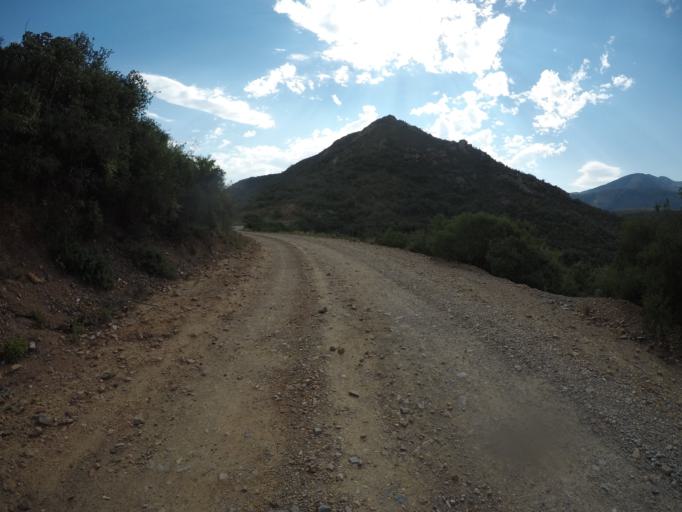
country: ZA
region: Eastern Cape
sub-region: Cacadu District Municipality
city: Kareedouw
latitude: -33.6475
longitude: 24.3403
